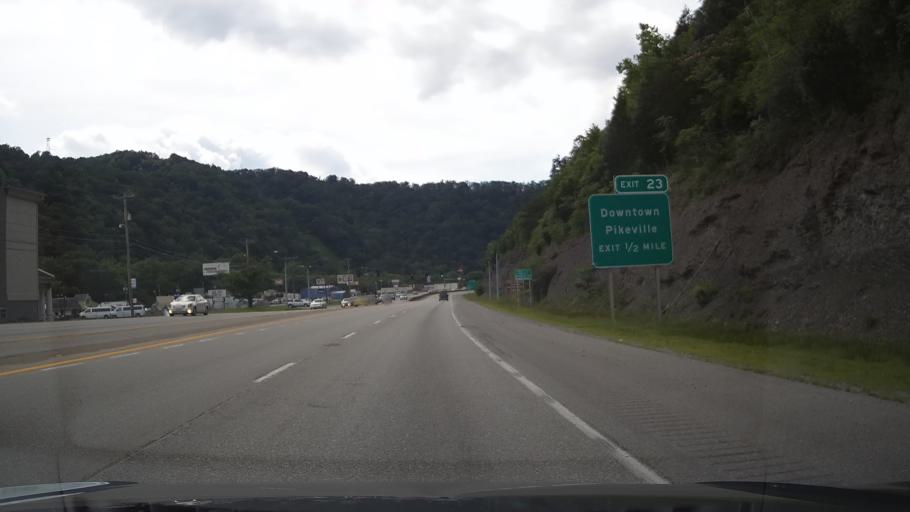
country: US
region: Kentucky
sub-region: Pike County
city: Pikeville
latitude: 37.4655
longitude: -82.5261
